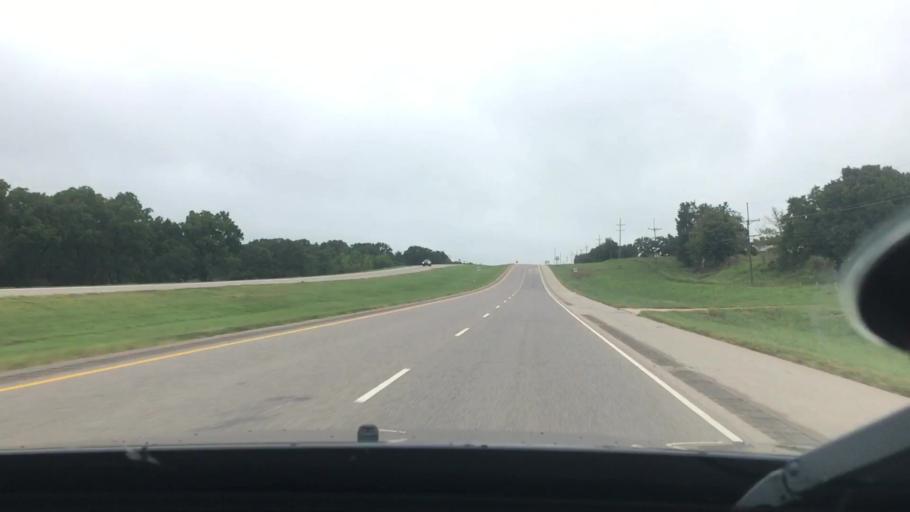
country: US
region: Oklahoma
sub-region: Seminole County
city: Seminole
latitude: 35.3412
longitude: -96.6715
